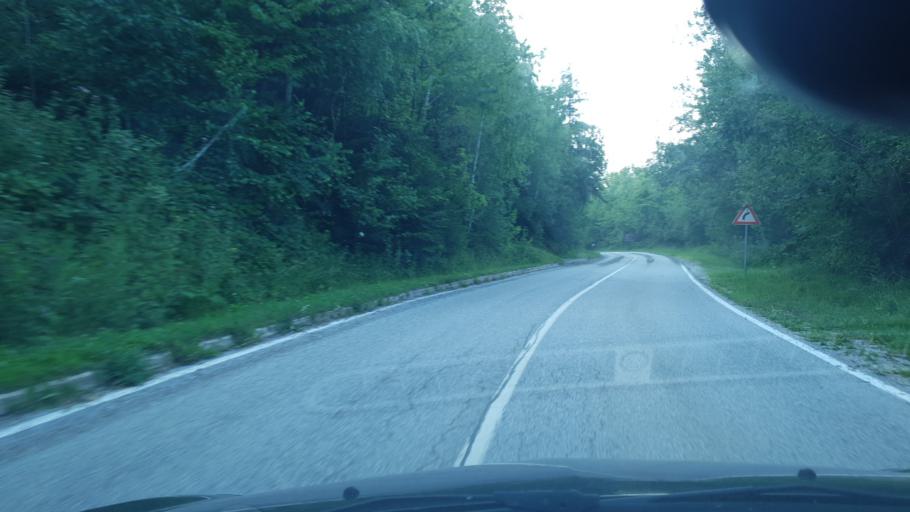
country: HR
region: Grad Zagreb
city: Kasina
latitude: 45.9192
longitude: 15.9685
